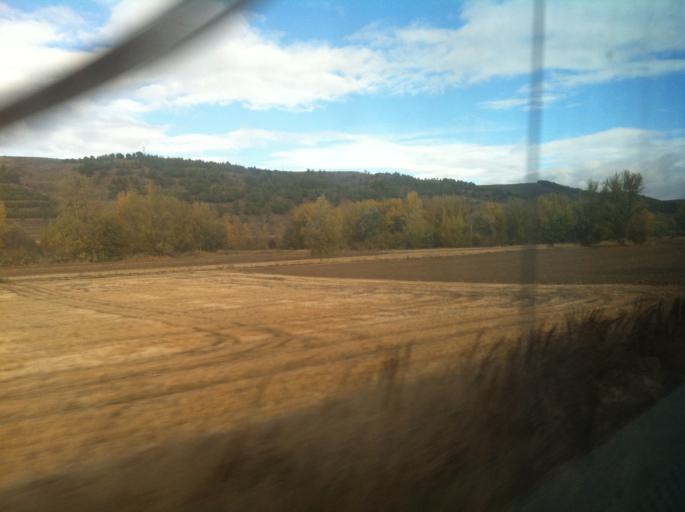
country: ES
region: Castille and Leon
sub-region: Provincia de Burgos
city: Pradanos de Bureba
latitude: 42.5055
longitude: -3.3442
